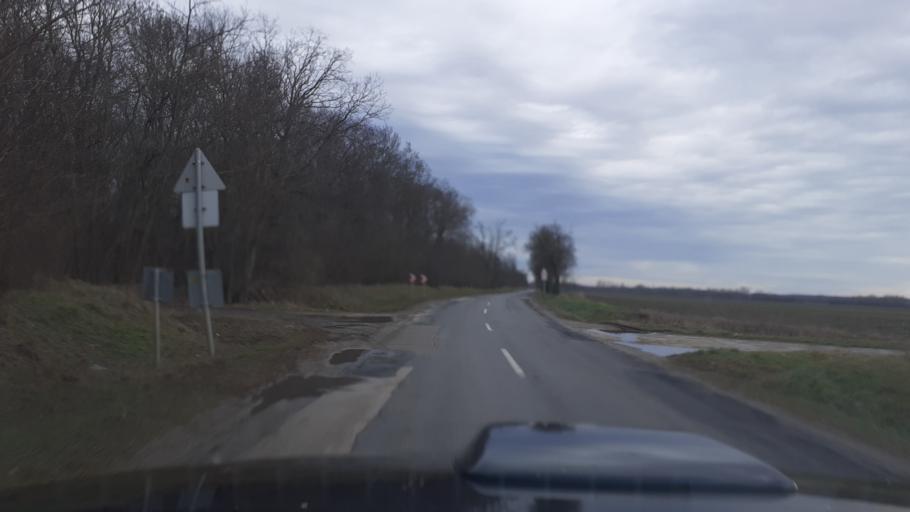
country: HU
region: Fejer
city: Sarosd
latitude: 47.0243
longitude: 18.6733
